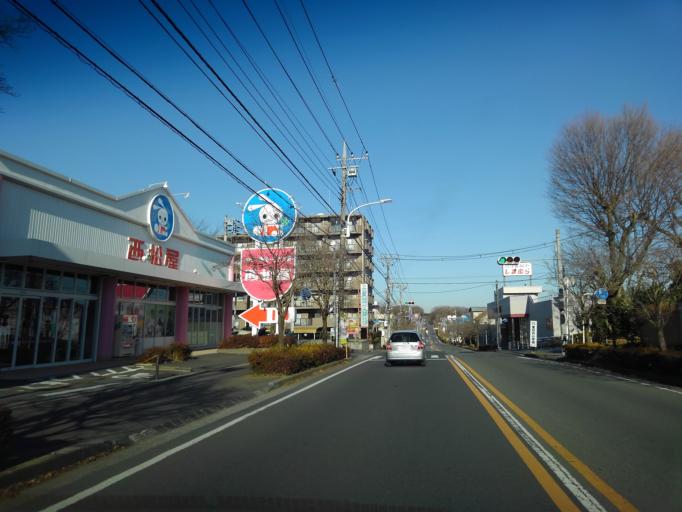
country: JP
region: Saitama
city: Tokorozawa
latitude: 35.7984
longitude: 139.5110
